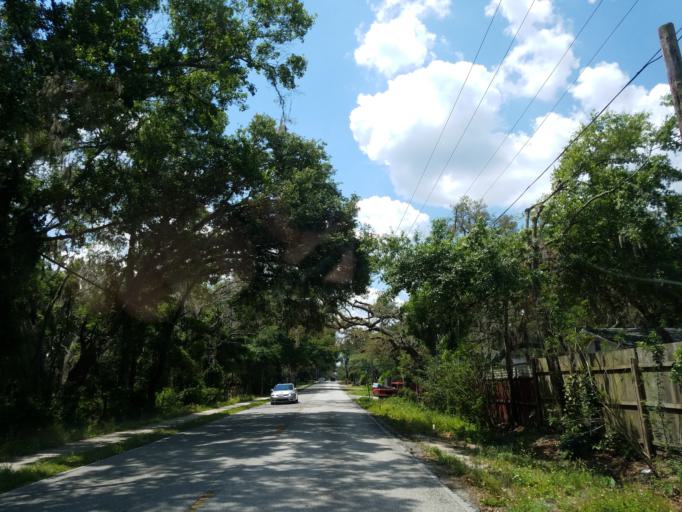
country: US
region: Florida
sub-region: Hillsborough County
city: Bloomingdale
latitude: 27.8874
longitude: -82.2858
